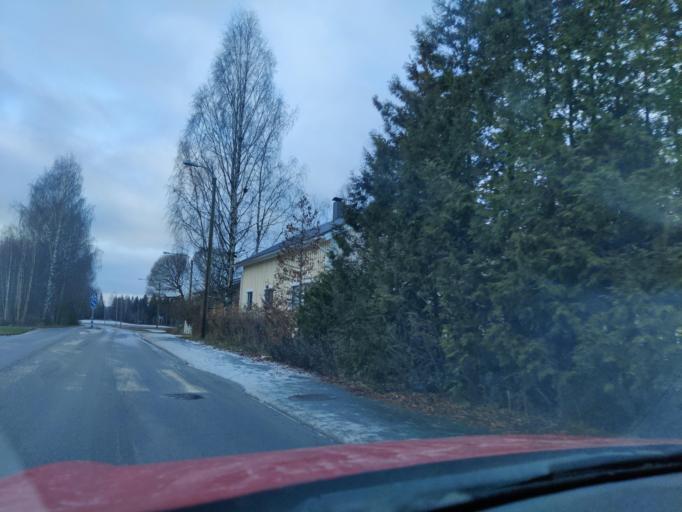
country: FI
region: Pirkanmaa
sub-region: Tampere
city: Nokia
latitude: 61.4645
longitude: 23.4777
